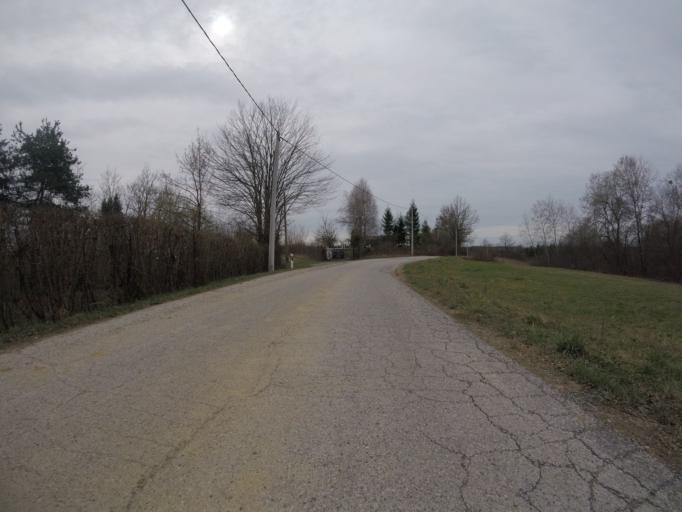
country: HR
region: Zagrebacka
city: Lukavec
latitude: 45.5725
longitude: 15.9647
